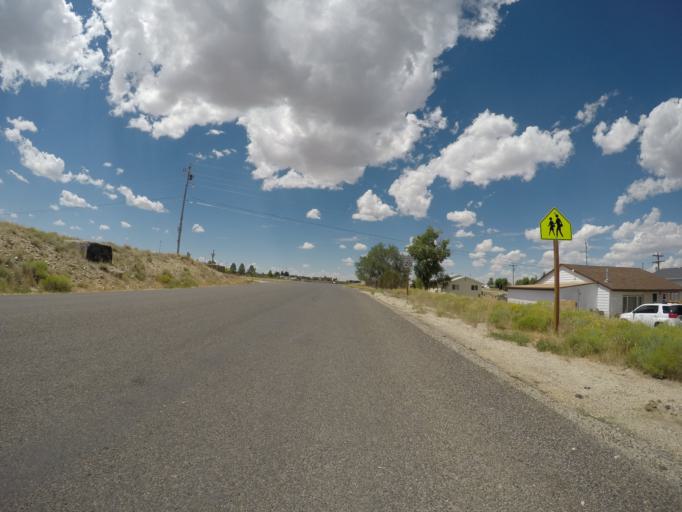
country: US
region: Wyoming
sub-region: Carbon County
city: Saratoga
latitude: 41.4529
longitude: -106.8169
